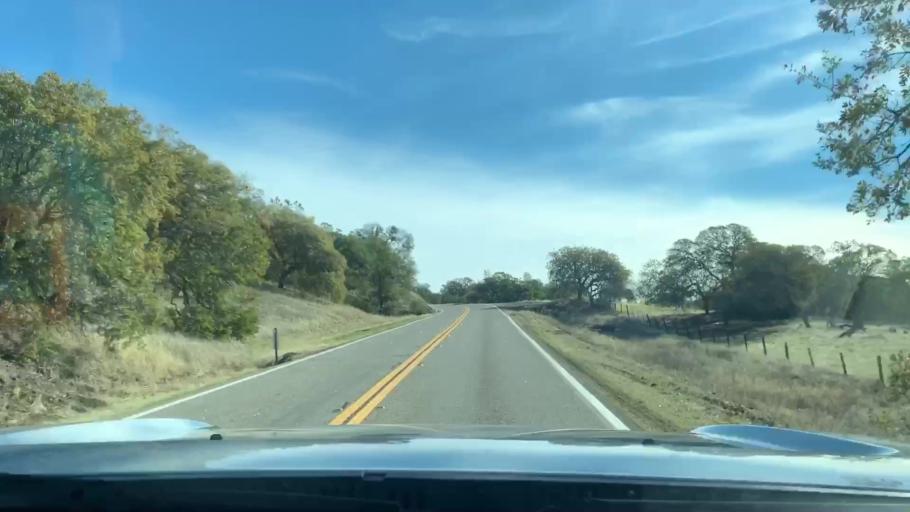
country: US
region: California
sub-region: Monterey County
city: King City
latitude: 36.1934
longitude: -120.7658
